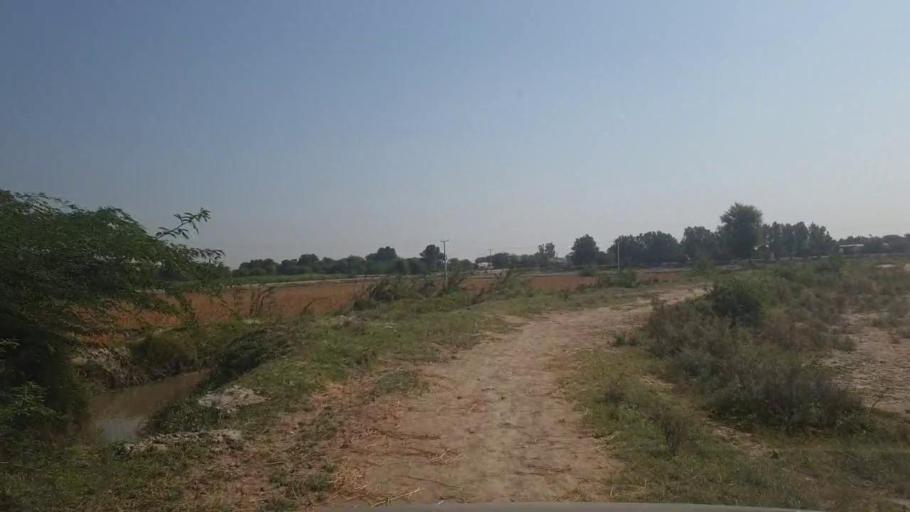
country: PK
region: Sindh
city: Badin
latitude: 24.6789
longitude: 68.9002
